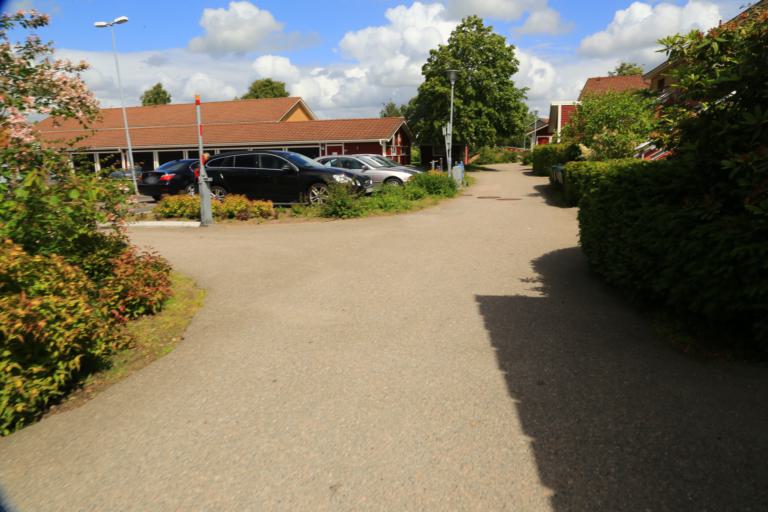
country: SE
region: Halland
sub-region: Varbergs Kommun
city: Varberg
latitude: 57.1124
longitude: 12.2803
